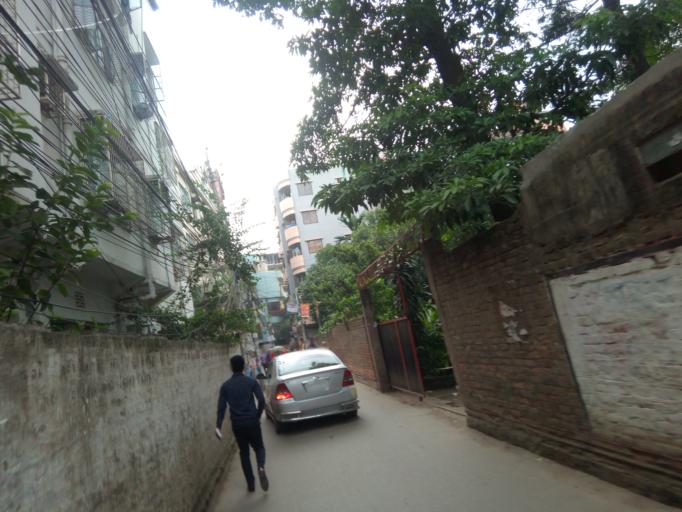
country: BD
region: Dhaka
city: Azimpur
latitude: 23.7541
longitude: 90.3845
